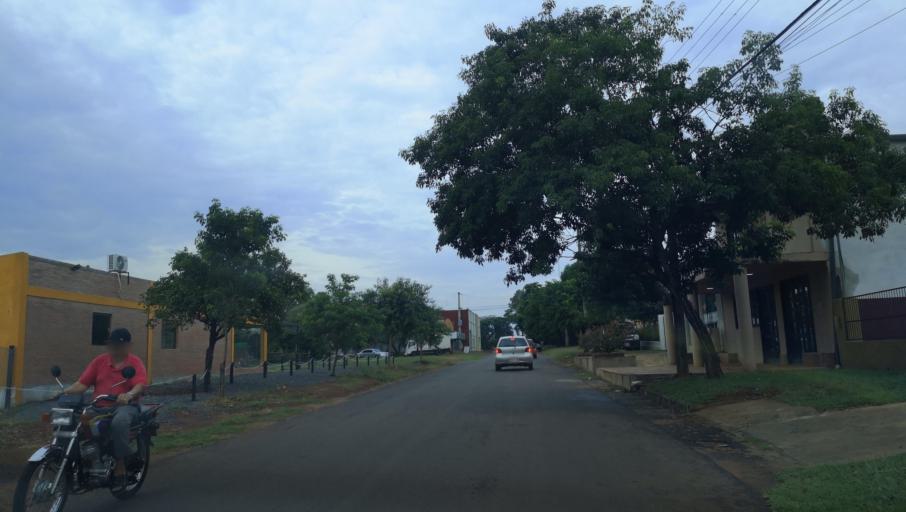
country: PY
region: Misiones
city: Santa Maria
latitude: -26.8838
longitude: -57.0345
